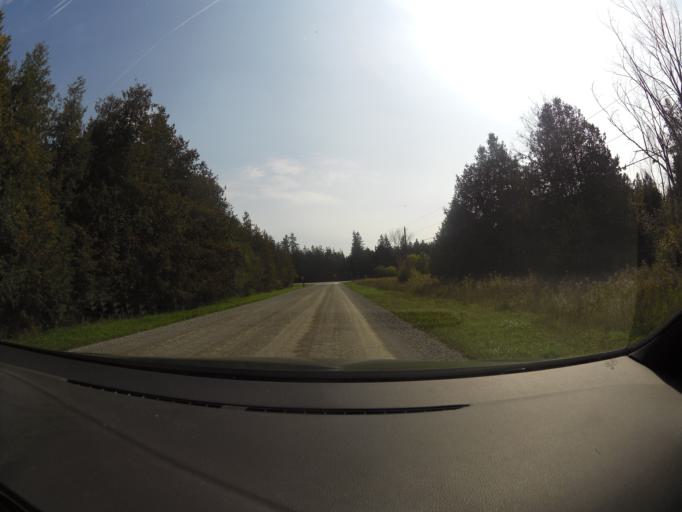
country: CA
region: Ontario
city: Carleton Place
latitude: 45.3263
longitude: -76.1754
